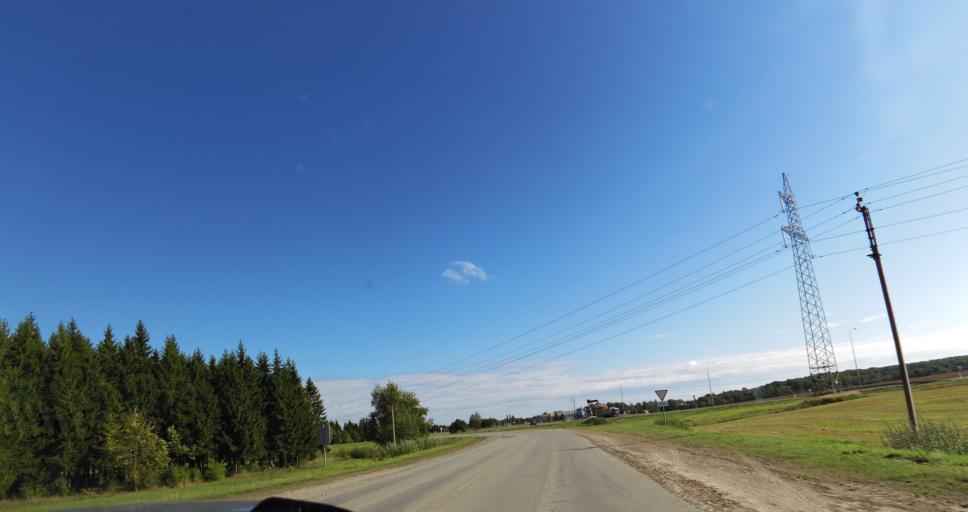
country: LT
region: Panevezys
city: Pasvalys
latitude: 56.0663
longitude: 24.4288
